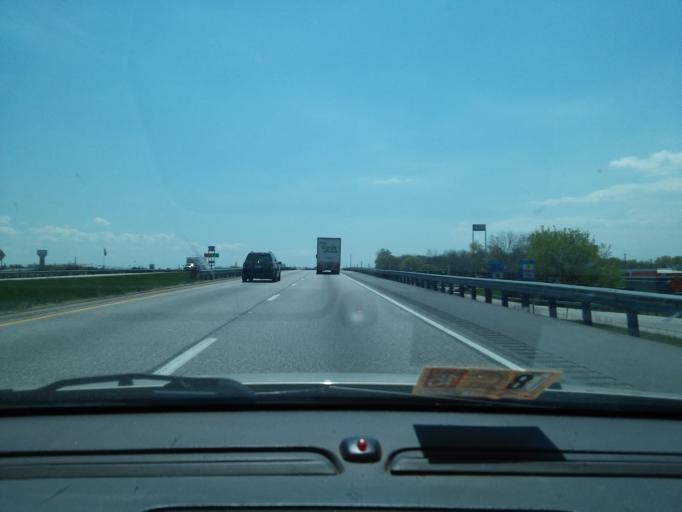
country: US
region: Pennsylvania
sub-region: Franklin County
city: Greencastle
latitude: 39.7884
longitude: -77.7127
